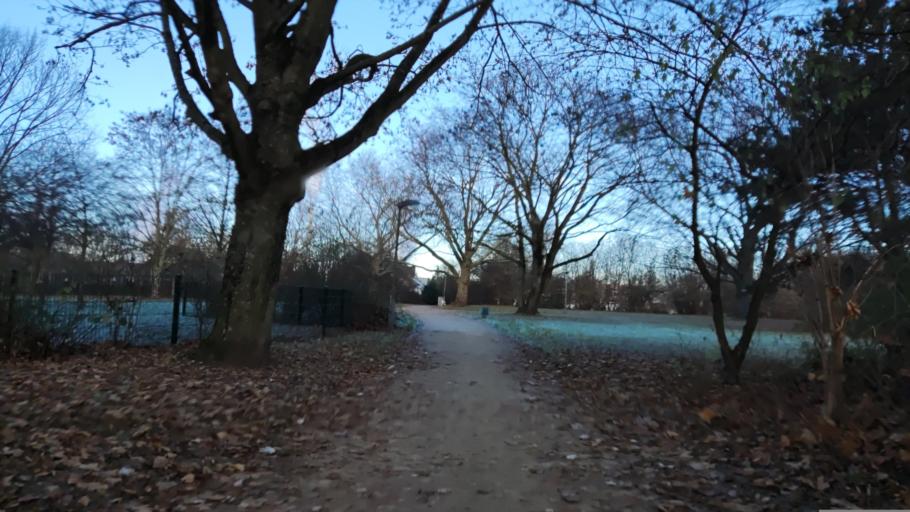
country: DE
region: North Rhine-Westphalia
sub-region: Regierungsbezirk Arnsberg
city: Herne
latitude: 51.5336
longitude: 7.2001
